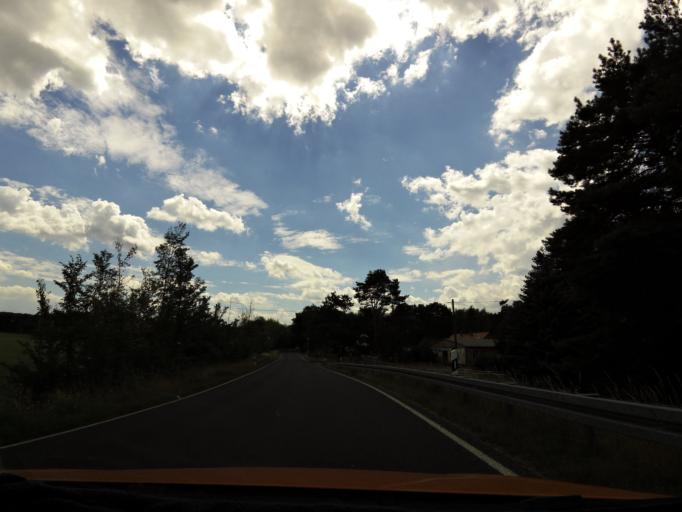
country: DE
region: Brandenburg
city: Munchehofe
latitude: 52.2536
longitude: 13.7913
